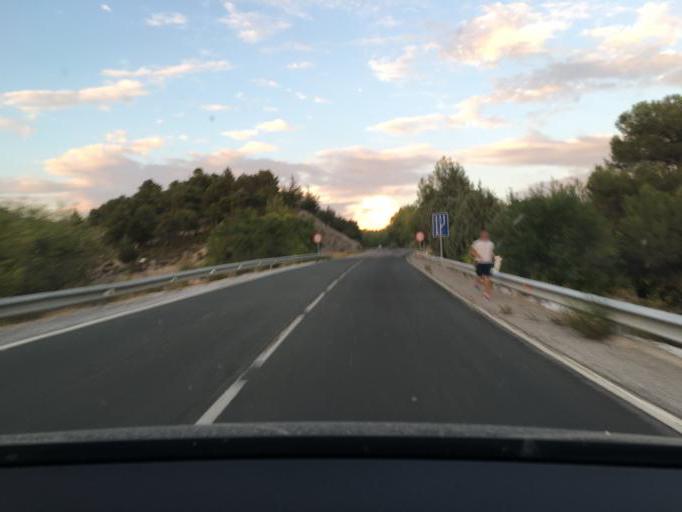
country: ES
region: Andalusia
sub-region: Provincia de Granada
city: Viznar
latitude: 37.2186
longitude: -3.5430
